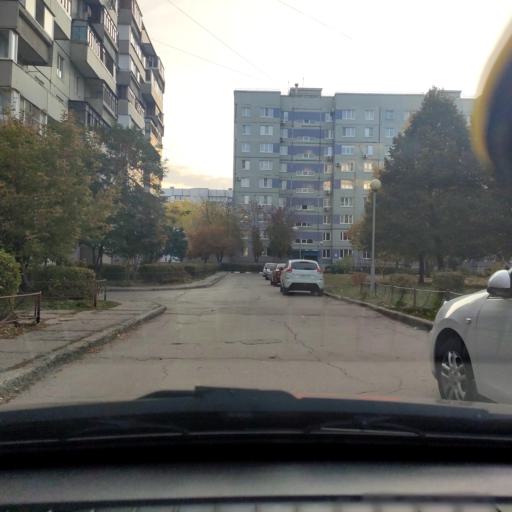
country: RU
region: Samara
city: Tol'yatti
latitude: 53.5354
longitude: 49.3418
